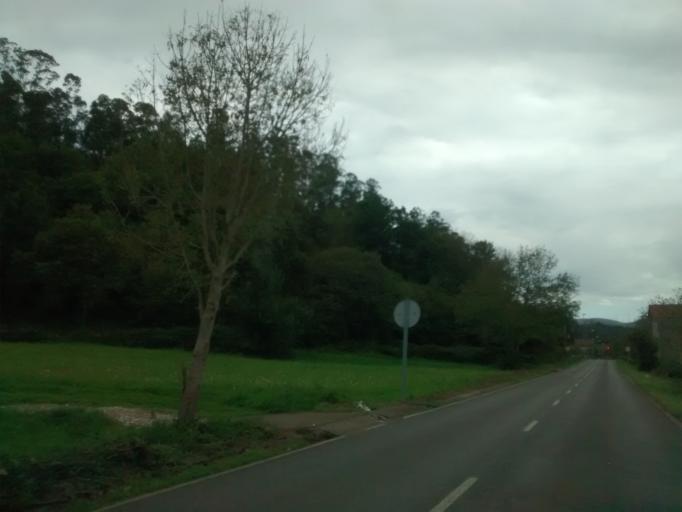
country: ES
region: Cantabria
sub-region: Provincia de Cantabria
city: Entrambasaguas
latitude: 43.3443
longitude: -3.6803
